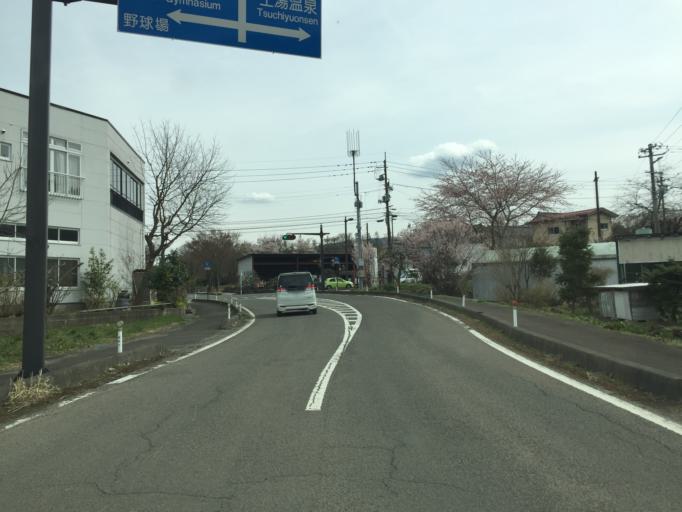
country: JP
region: Fukushima
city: Fukushima-shi
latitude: 37.7215
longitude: 140.3567
